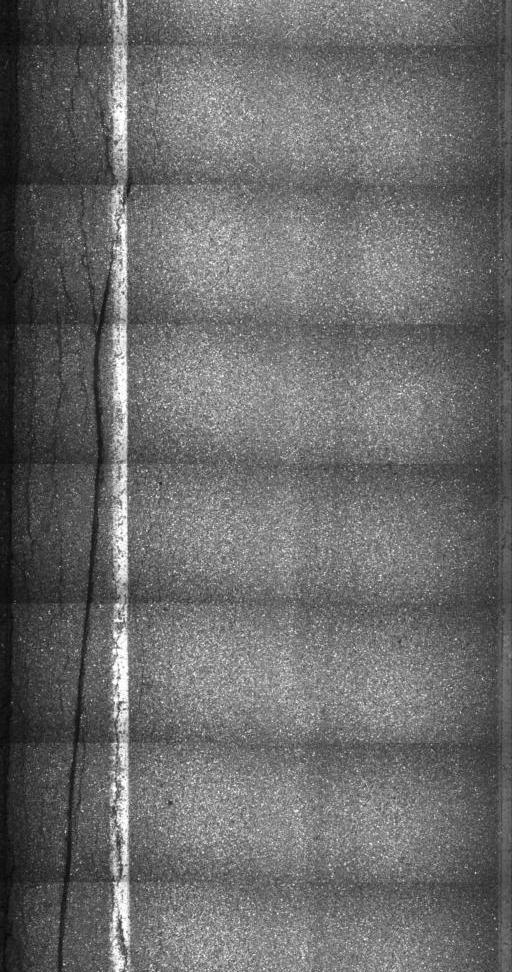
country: US
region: Vermont
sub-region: Orange County
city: Randolph
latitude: 43.8489
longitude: -72.8580
